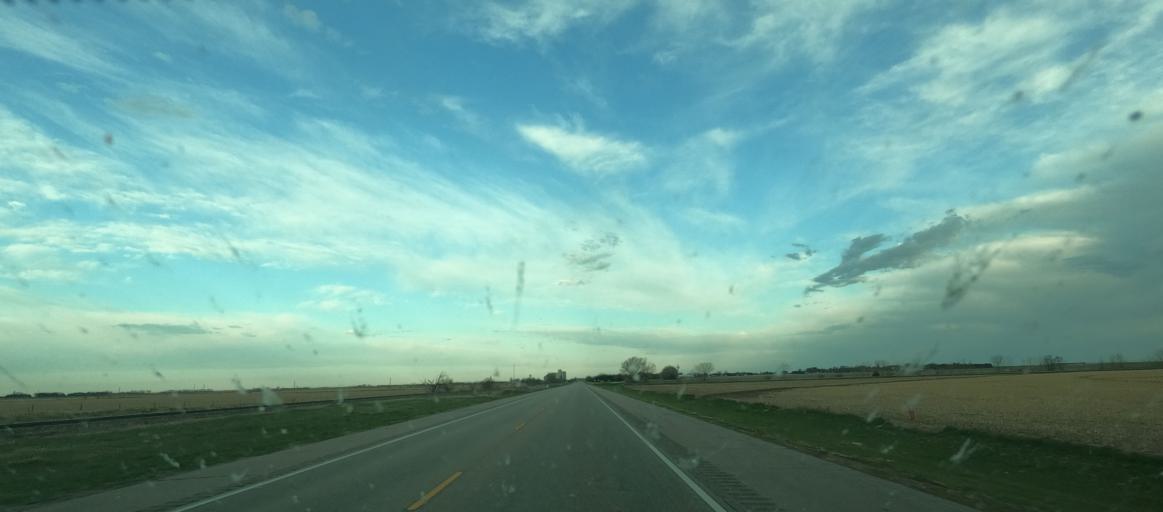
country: US
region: Nebraska
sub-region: Kearney County
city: Minden
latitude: 40.4820
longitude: -99.0992
